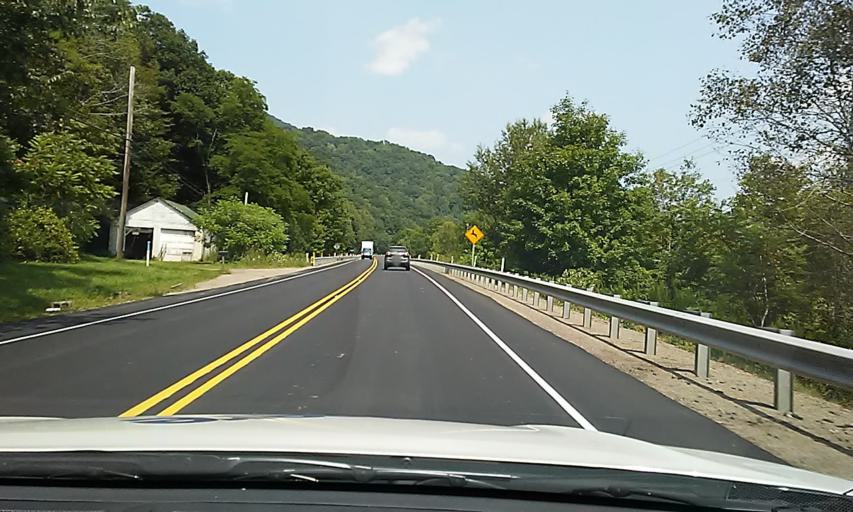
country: US
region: Pennsylvania
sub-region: Cameron County
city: Emporium
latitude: 41.4790
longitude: -78.3230
